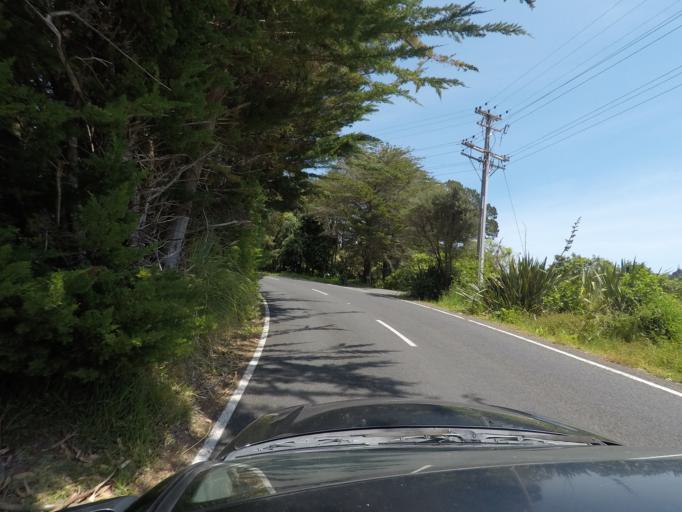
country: NZ
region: Auckland
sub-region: Auckland
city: Titirangi
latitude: -36.9681
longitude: 174.6406
